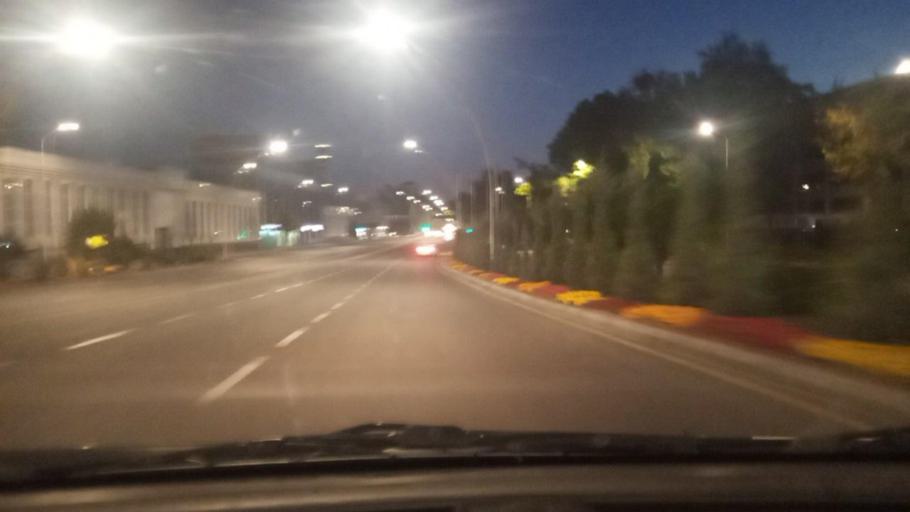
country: UZ
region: Toshkent Shahri
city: Tashkent
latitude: 41.2700
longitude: 69.2607
